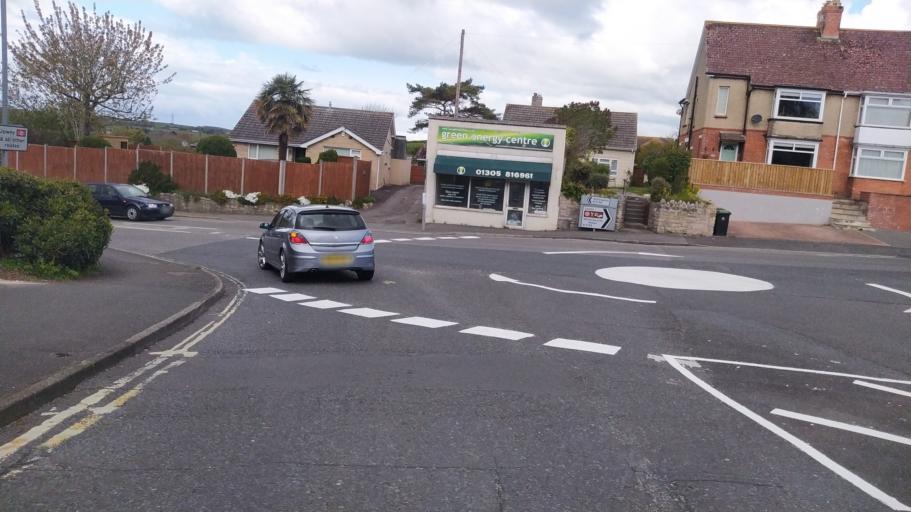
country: GB
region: England
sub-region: Dorset
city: Weymouth
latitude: 50.6514
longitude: -2.4702
